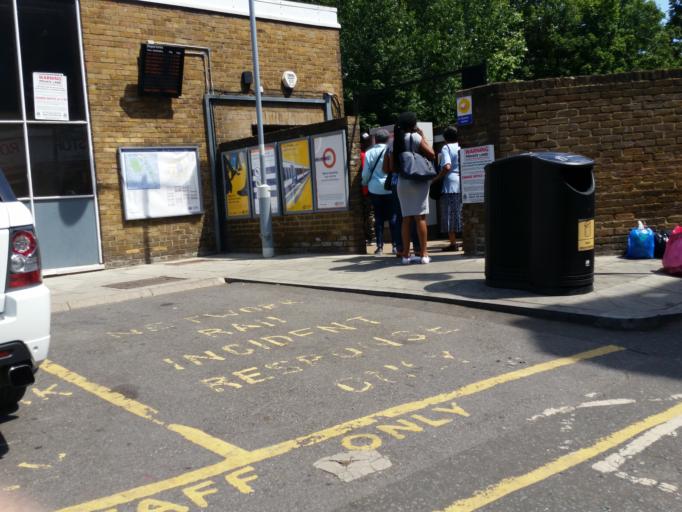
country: GB
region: England
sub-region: Greater London
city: Hackney
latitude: 51.5652
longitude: -0.0730
